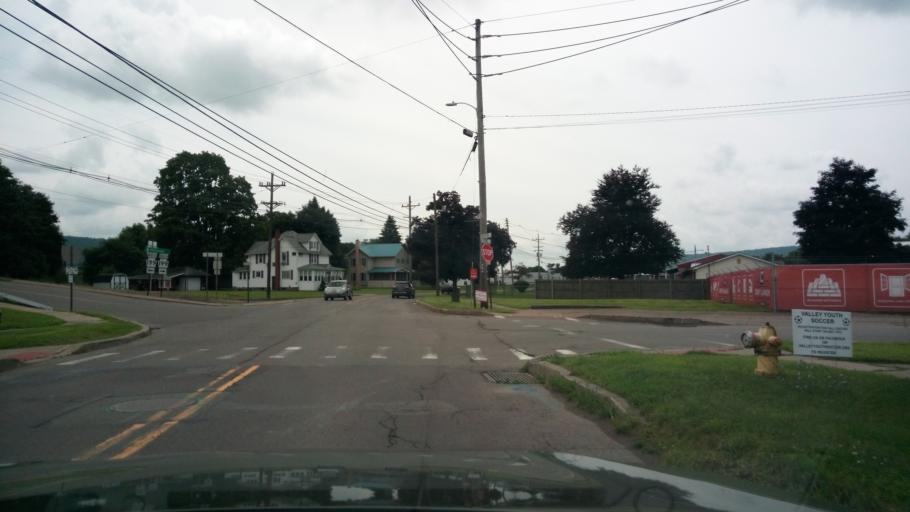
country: US
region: Pennsylvania
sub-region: Bradford County
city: South Waverly
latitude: 41.9942
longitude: -76.5215
